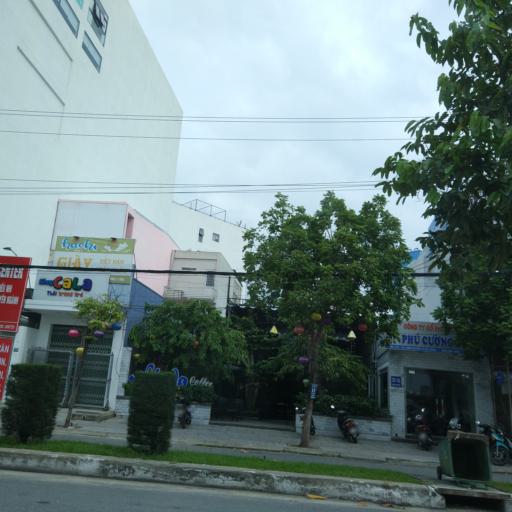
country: VN
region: Da Nang
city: Son Tra
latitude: 16.0695
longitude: 108.2319
